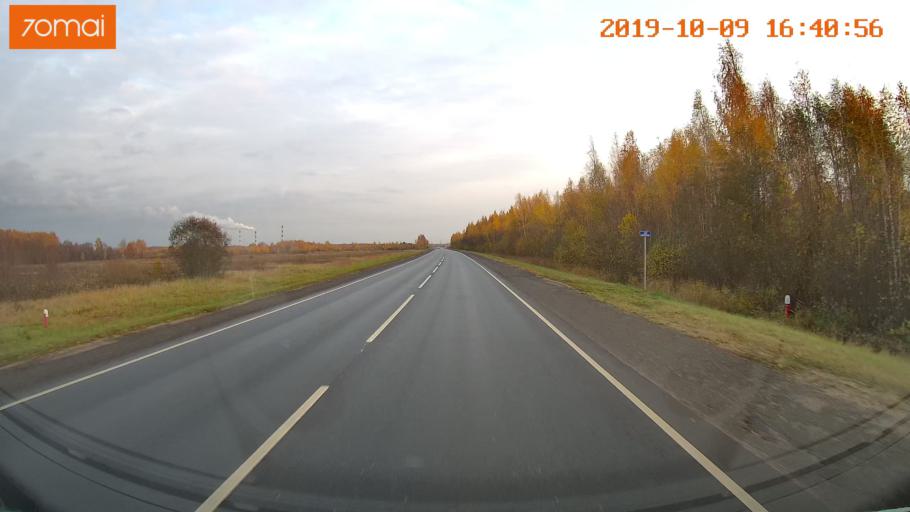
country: RU
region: Kostroma
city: Volgorechensk
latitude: 57.4778
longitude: 41.0702
